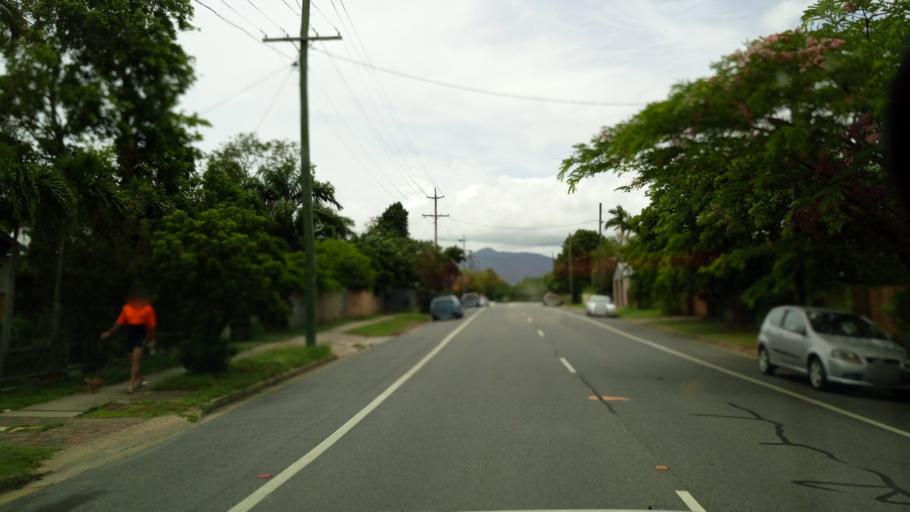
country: AU
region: Queensland
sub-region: Cairns
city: Yorkeys Knob
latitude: -16.8523
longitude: 145.7474
